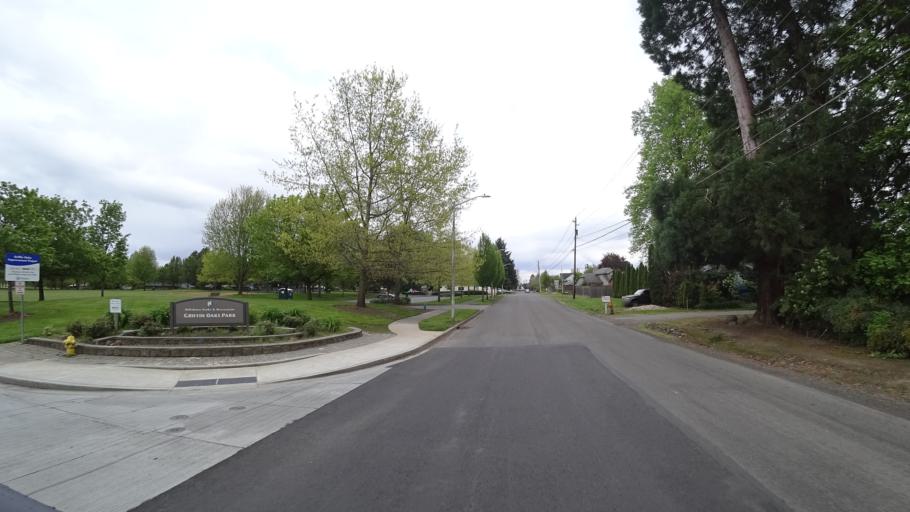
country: US
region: Oregon
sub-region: Washington County
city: Hillsboro
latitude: 45.5401
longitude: -122.9664
